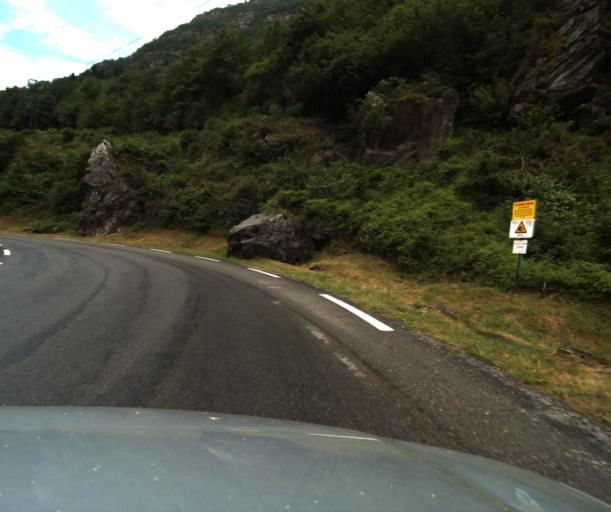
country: FR
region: Midi-Pyrenees
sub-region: Departement des Hautes-Pyrenees
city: Luz-Saint-Sauveur
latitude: 42.8377
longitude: -0.0033
